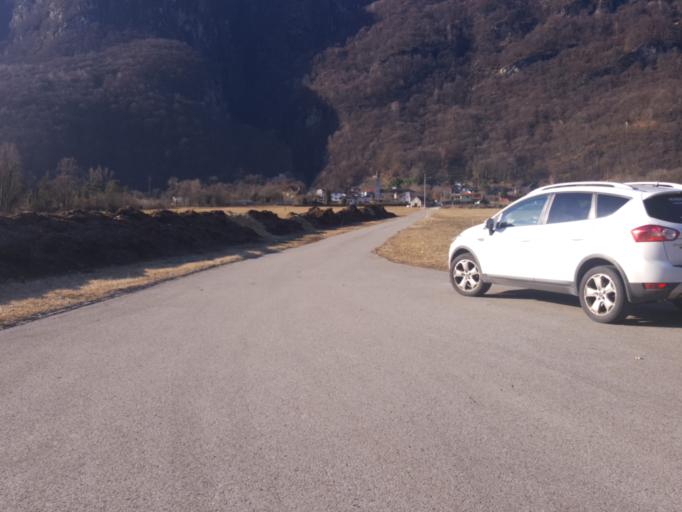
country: CH
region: Ticino
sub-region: Riviera District
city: Claro
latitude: 46.2714
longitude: 8.9998
